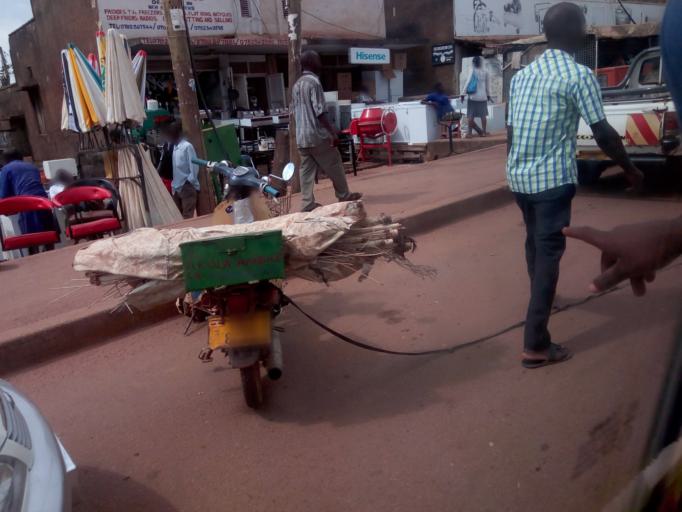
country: UG
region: Central Region
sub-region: Kampala District
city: Kampala
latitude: 0.2968
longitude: 32.5740
